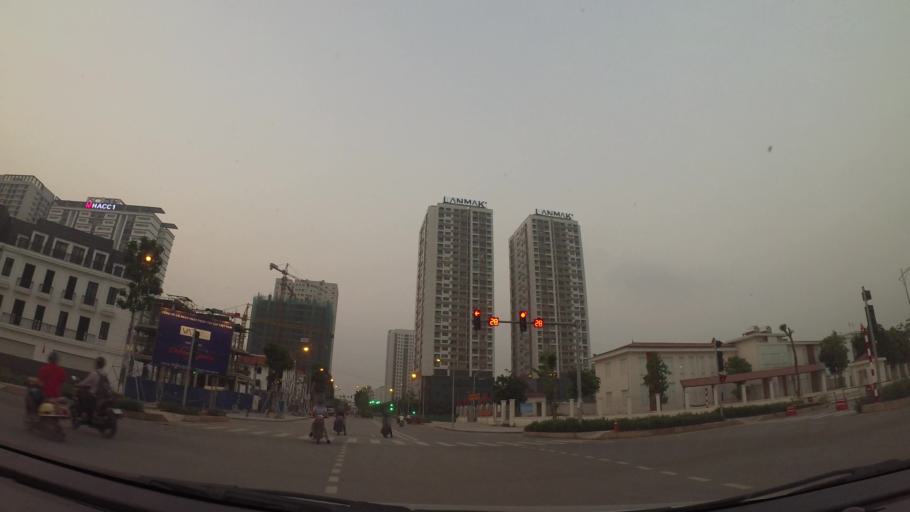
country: VN
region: Ha Noi
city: Tay Ho
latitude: 21.0627
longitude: 105.8007
